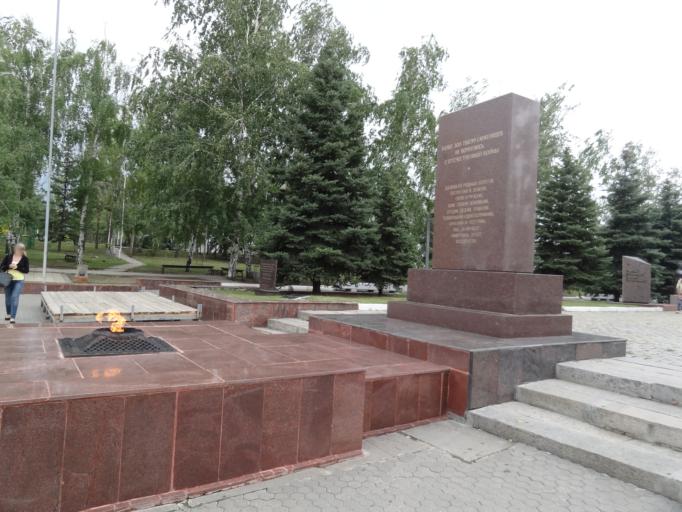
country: RU
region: Saratov
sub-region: Saratovskiy Rayon
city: Saratov
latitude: 51.5450
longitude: 46.0522
